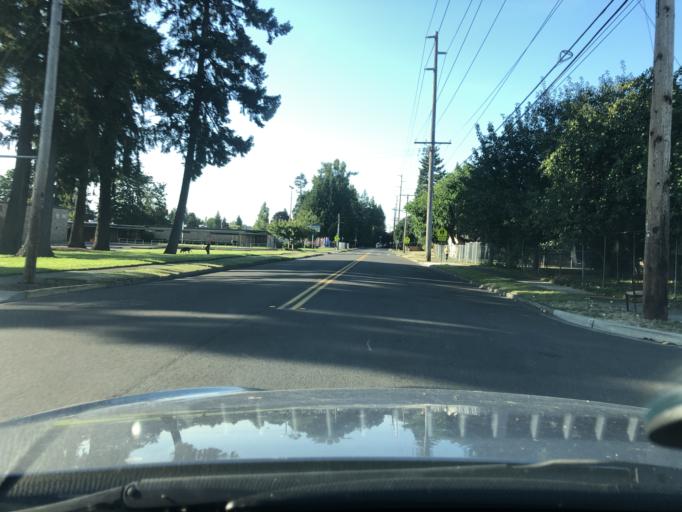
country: US
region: Washington
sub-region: King County
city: Auburn
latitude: 47.2873
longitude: -122.2134
